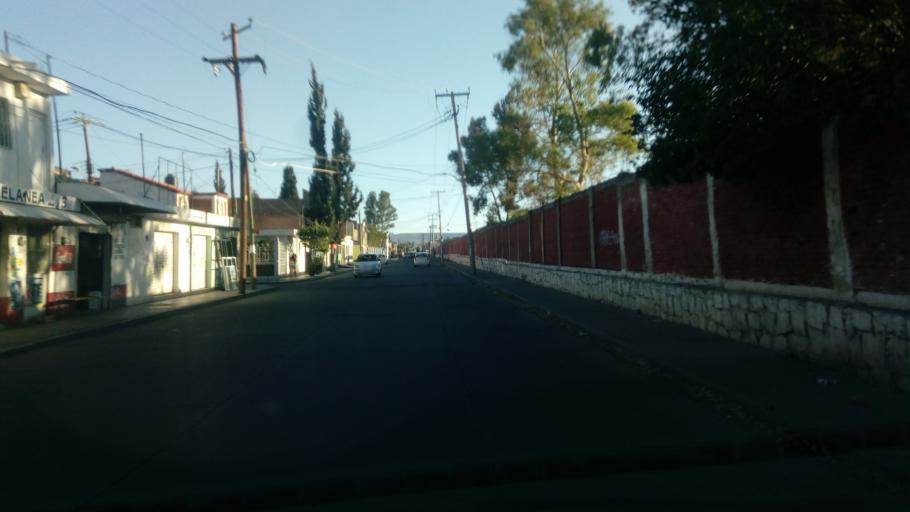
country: MX
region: Durango
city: Victoria de Durango
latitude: 24.0040
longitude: -104.6788
